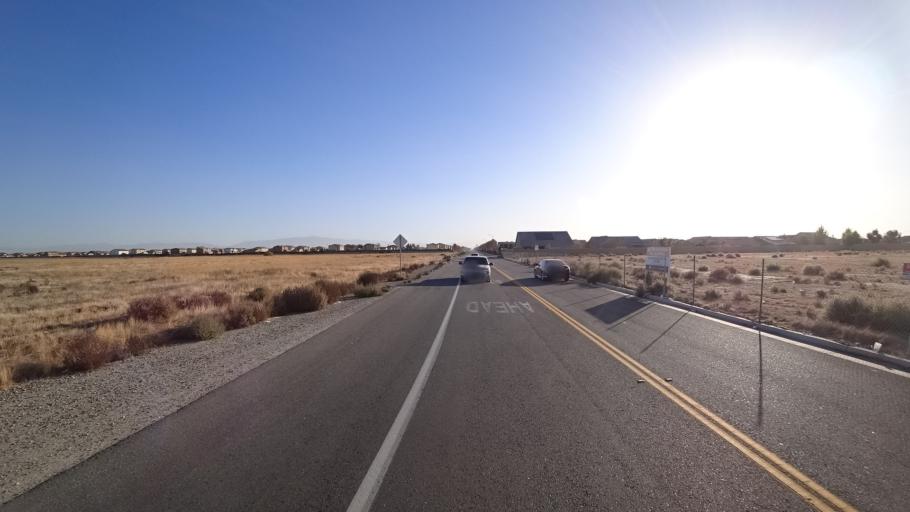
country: US
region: California
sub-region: Kern County
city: Greenfield
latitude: 35.2743
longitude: -119.0733
